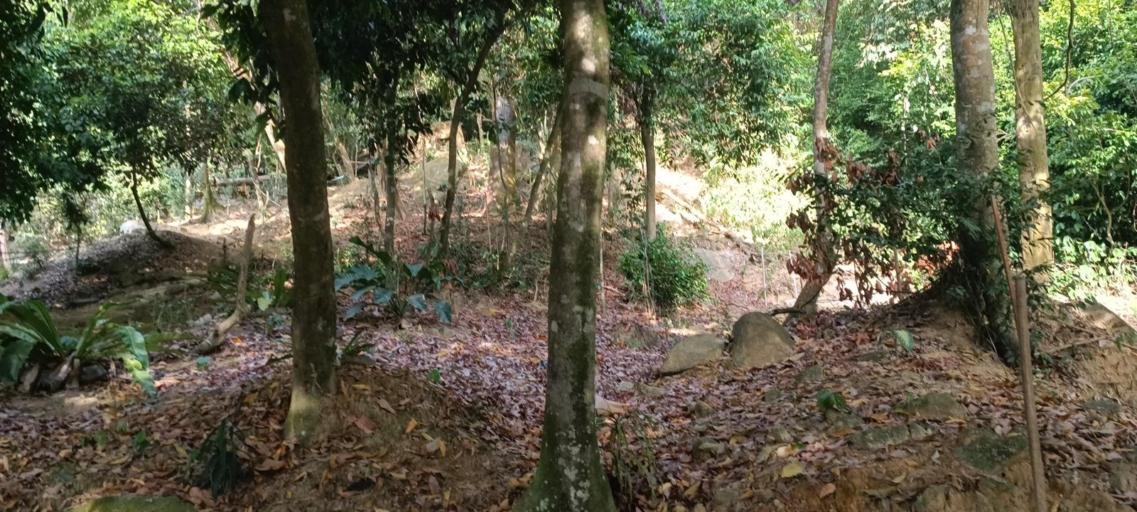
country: MY
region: Penang
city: Juru
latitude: 5.3352
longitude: 100.4135
